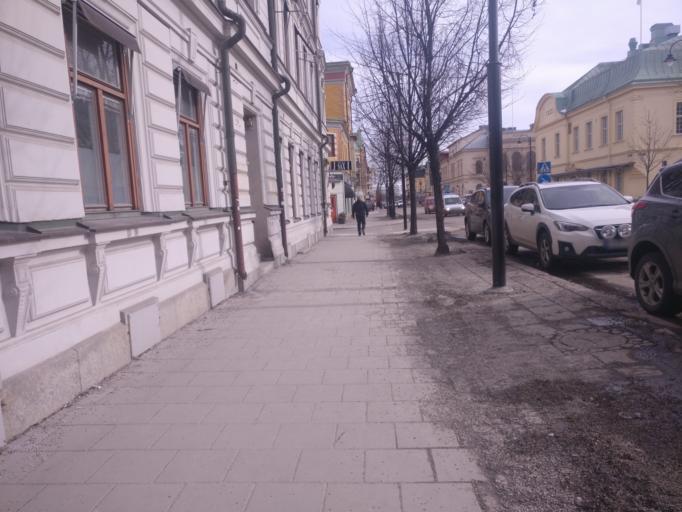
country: SE
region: Vaesternorrland
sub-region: Sundsvalls Kommun
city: Sundsvall
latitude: 62.3891
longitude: 17.3058
